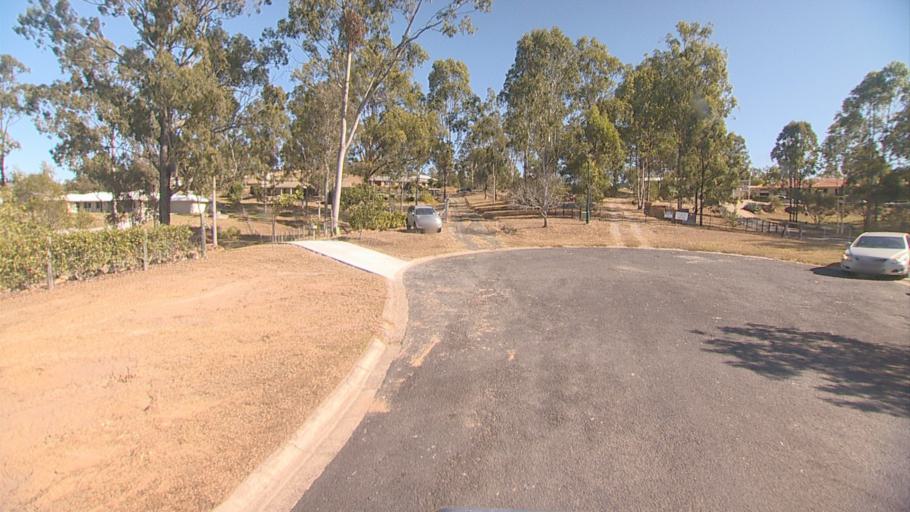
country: AU
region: Queensland
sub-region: Logan
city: Cedar Vale
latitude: -27.8686
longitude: 153.0365
